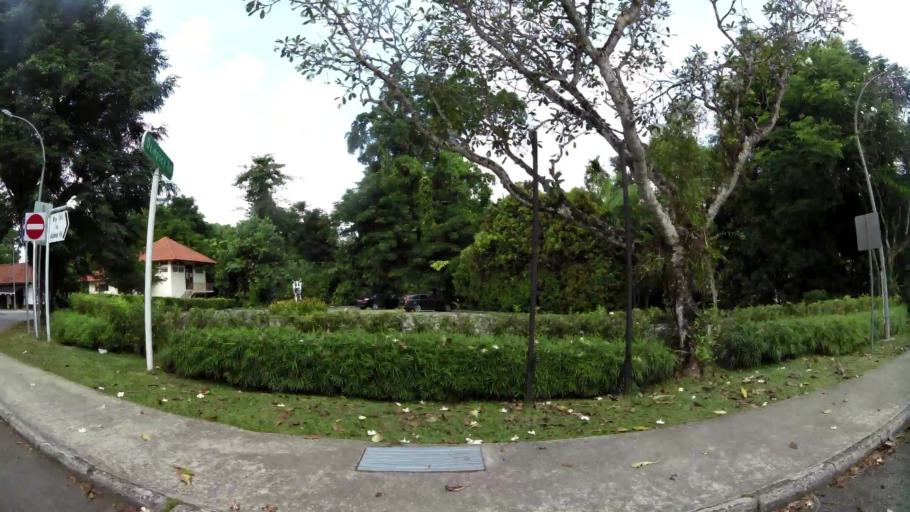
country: SG
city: Singapore
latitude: 1.3061
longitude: 103.8103
